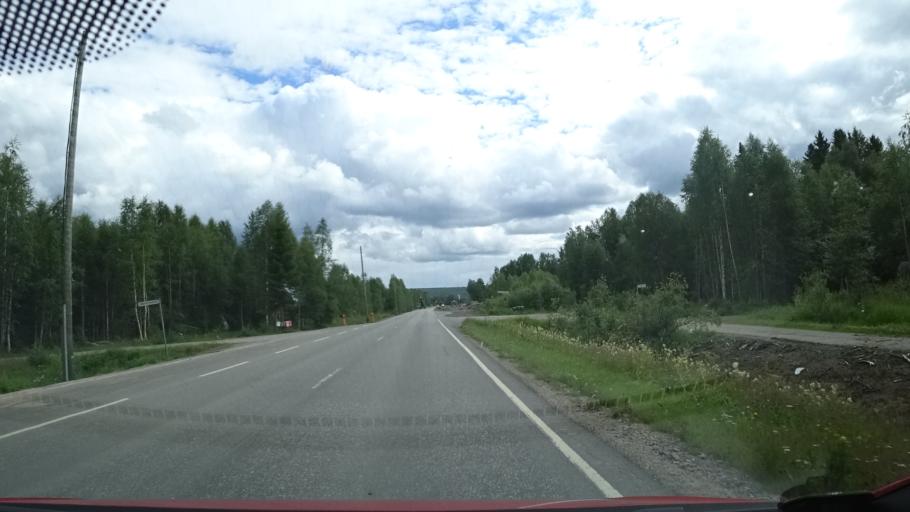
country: FI
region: Lapland
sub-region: Rovaniemi
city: Rovaniemi
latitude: 66.5299
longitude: 25.7380
